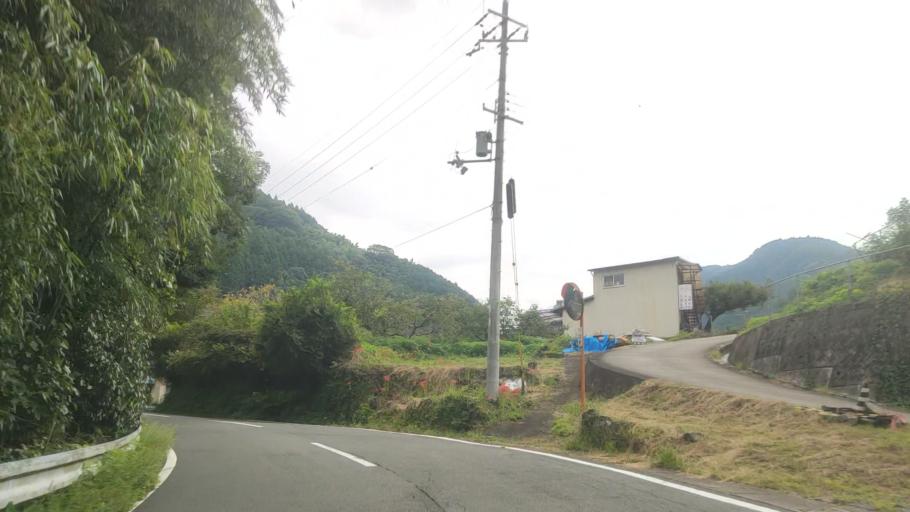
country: JP
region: Wakayama
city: Koya
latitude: 34.2598
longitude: 135.5466
